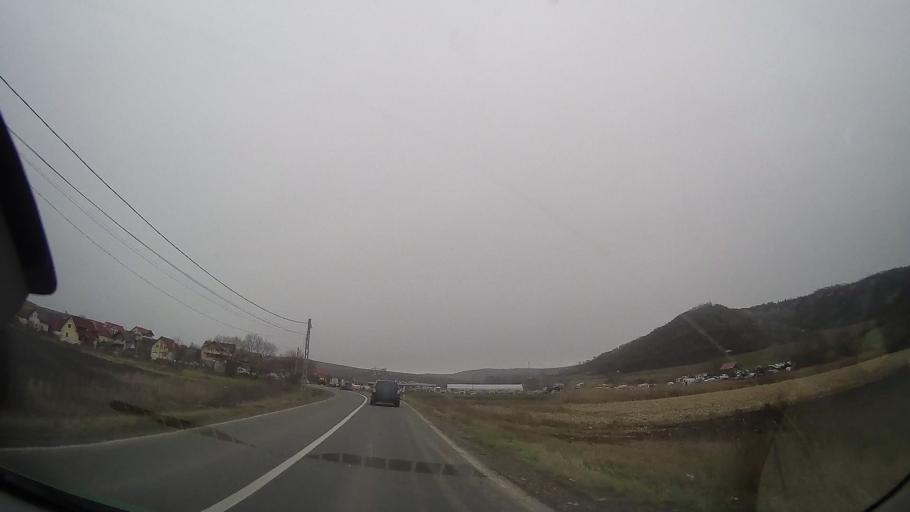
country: RO
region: Mures
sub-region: Comuna Ceausu de Campie
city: Ceausu de Campie
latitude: 46.6308
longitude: 24.5194
